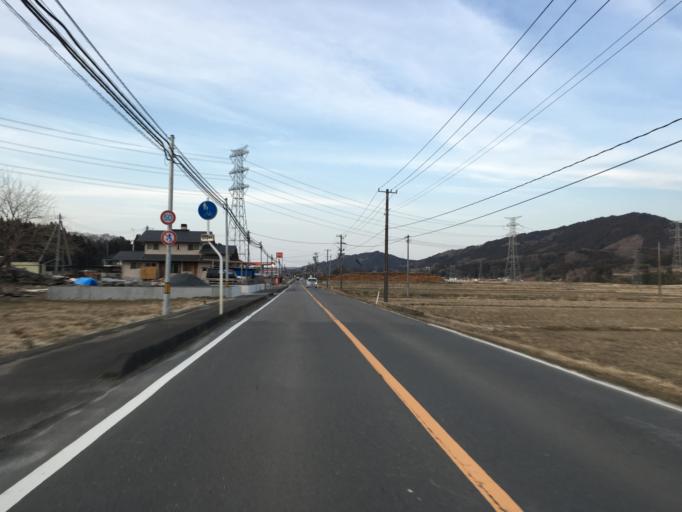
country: JP
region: Ibaraki
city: Daigo
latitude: 36.9236
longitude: 140.4080
